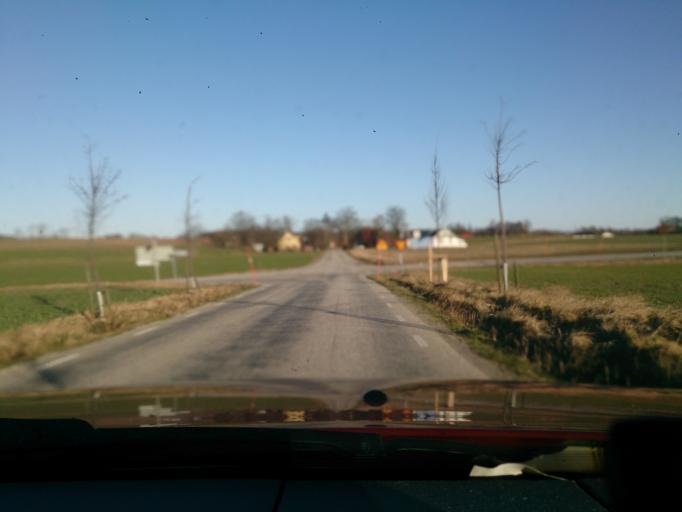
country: SE
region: Skane
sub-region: Skurups Kommun
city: Rydsgard
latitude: 55.4425
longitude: 13.6869
